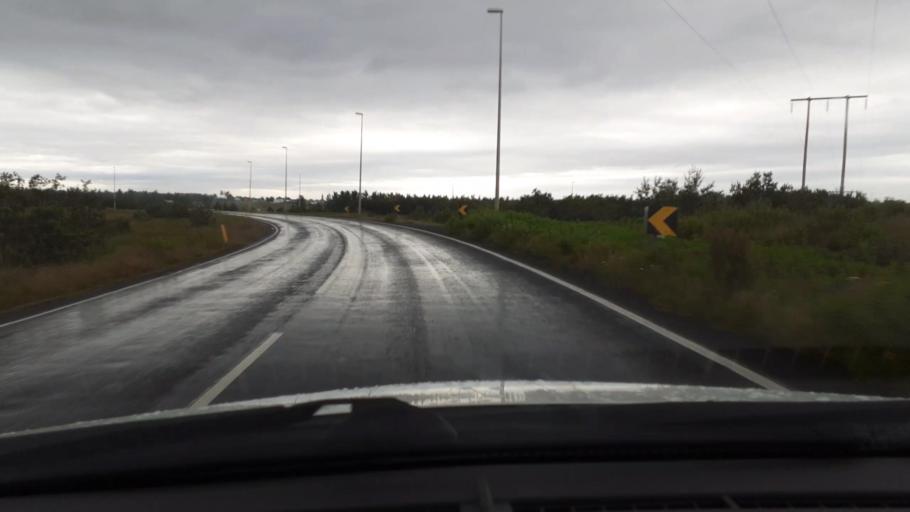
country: IS
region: West
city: Akranes
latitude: 64.3307
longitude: -22.0377
